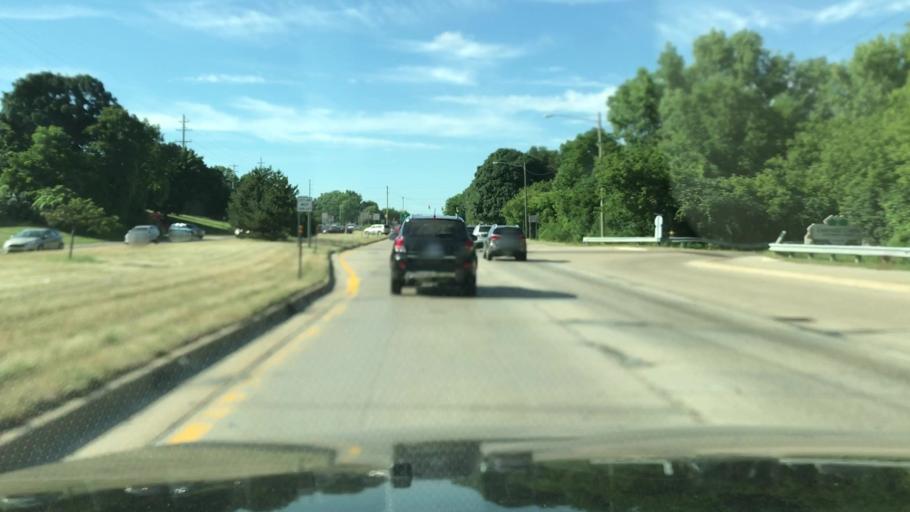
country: US
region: Michigan
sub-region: Kent County
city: East Grand Rapids
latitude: 42.9237
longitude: -85.5843
